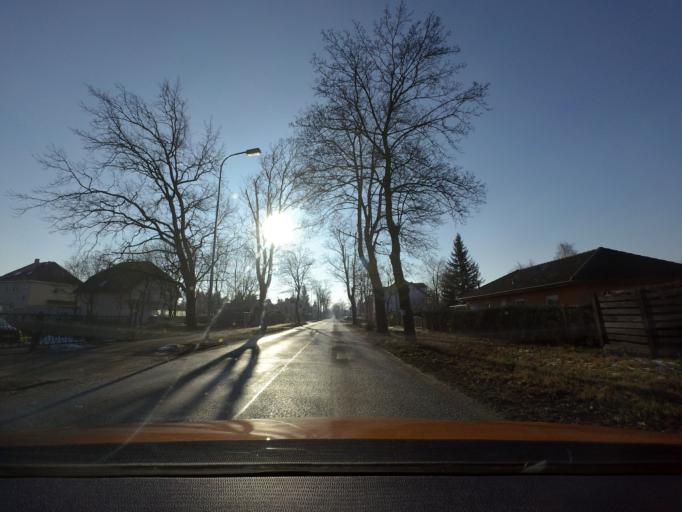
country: DE
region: Brandenburg
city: Falkensee
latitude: 52.5513
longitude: 13.0879
